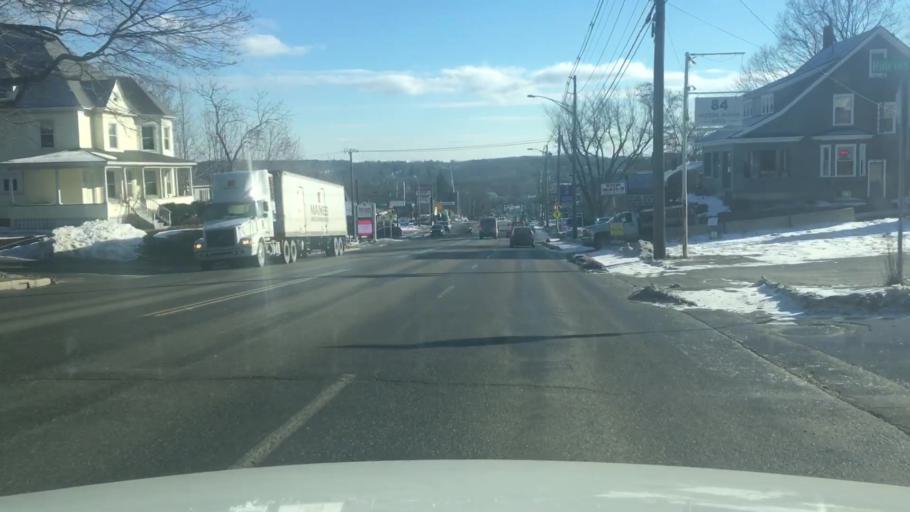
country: US
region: Maine
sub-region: Kennebec County
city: Augusta
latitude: 44.3121
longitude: -69.7894
